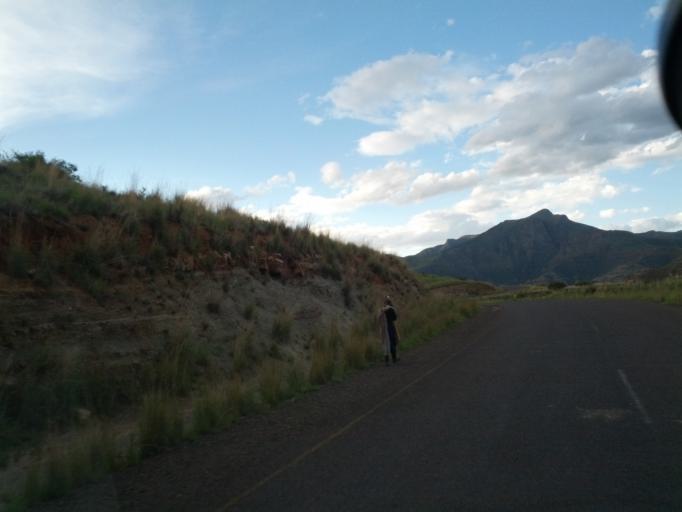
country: LS
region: Qacha's Nek
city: Qacha's Nek
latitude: -30.0776
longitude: 28.5800
